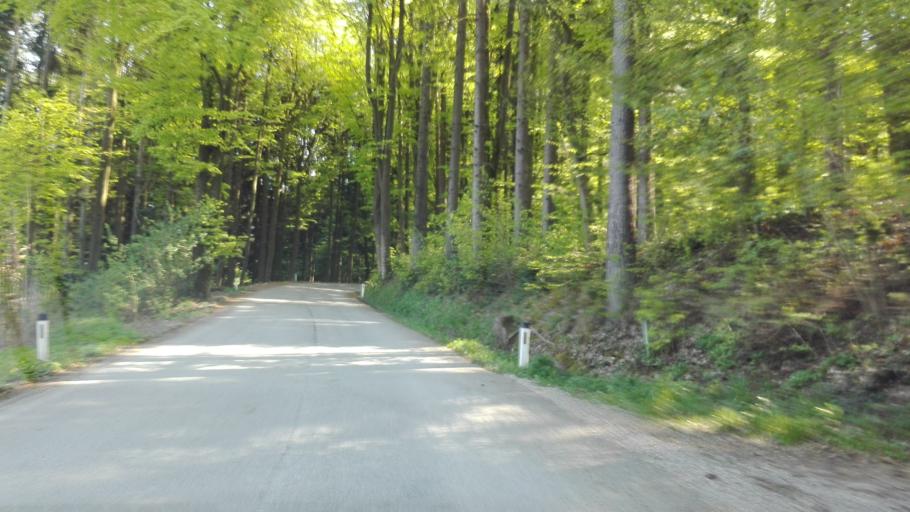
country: AT
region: Upper Austria
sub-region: Politischer Bezirk Rohrbach
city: Atzesberg
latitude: 48.4195
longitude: 13.9174
